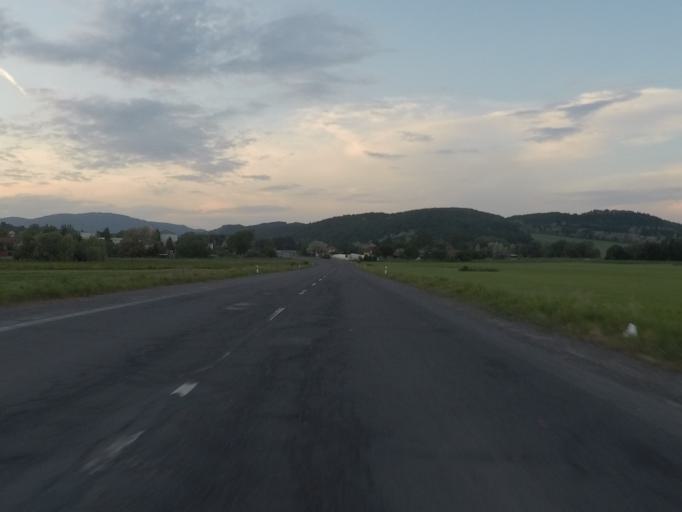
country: SK
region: Banskobystricky
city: Rimavska Sobota
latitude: 48.4604
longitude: 19.9533
